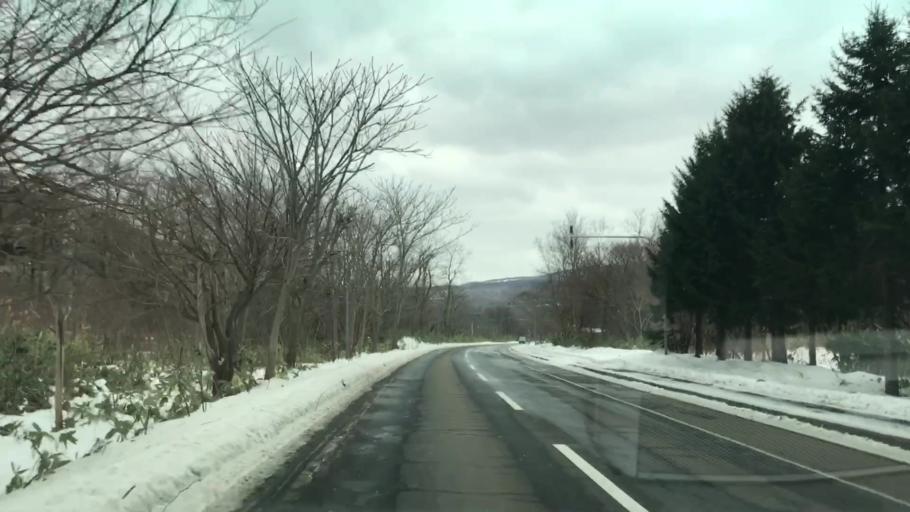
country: JP
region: Hokkaido
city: Yoichi
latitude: 43.3368
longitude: 140.4630
